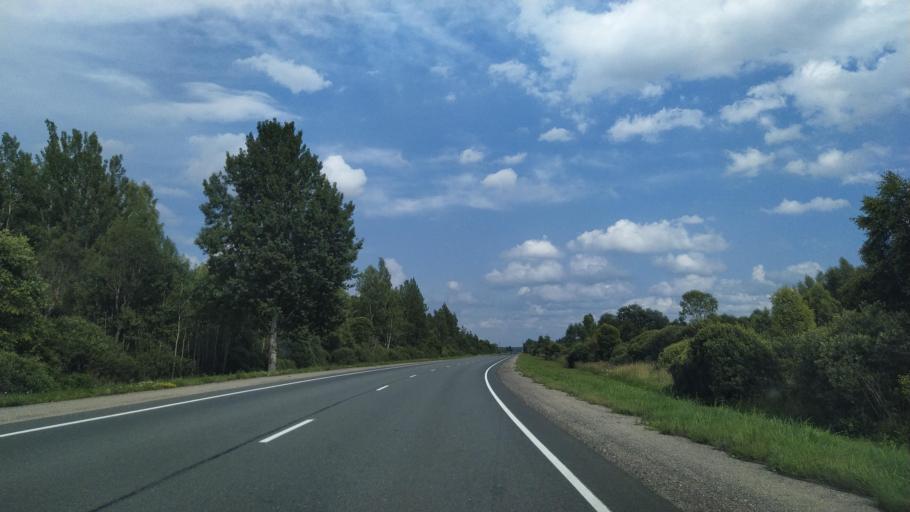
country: RU
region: Pskov
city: Porkhov
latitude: 57.9775
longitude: 29.7135
